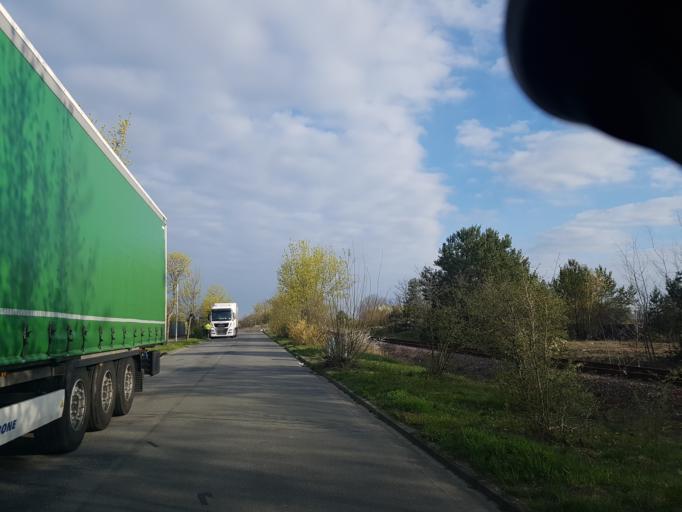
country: DE
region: Brandenburg
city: Bruck
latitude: 52.1772
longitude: 12.7746
